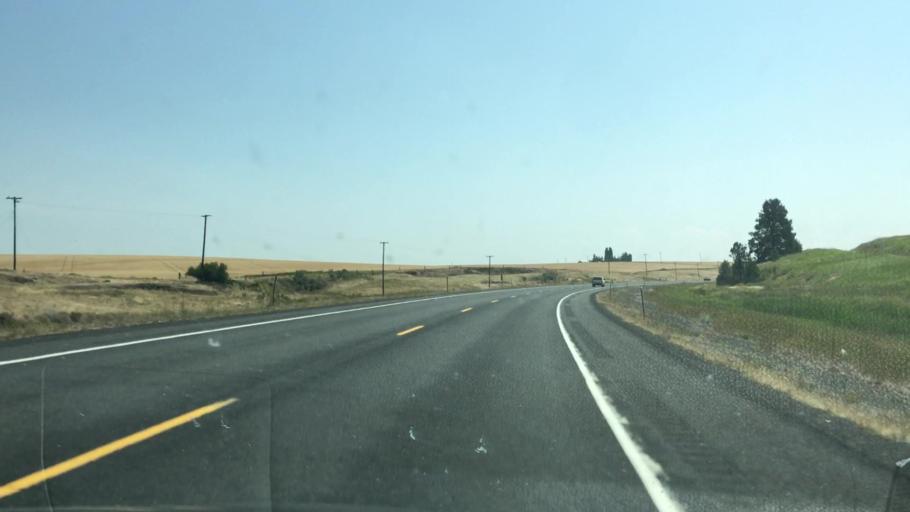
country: US
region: Idaho
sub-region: Lewis County
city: Nezperce
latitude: 46.2285
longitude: -116.4447
